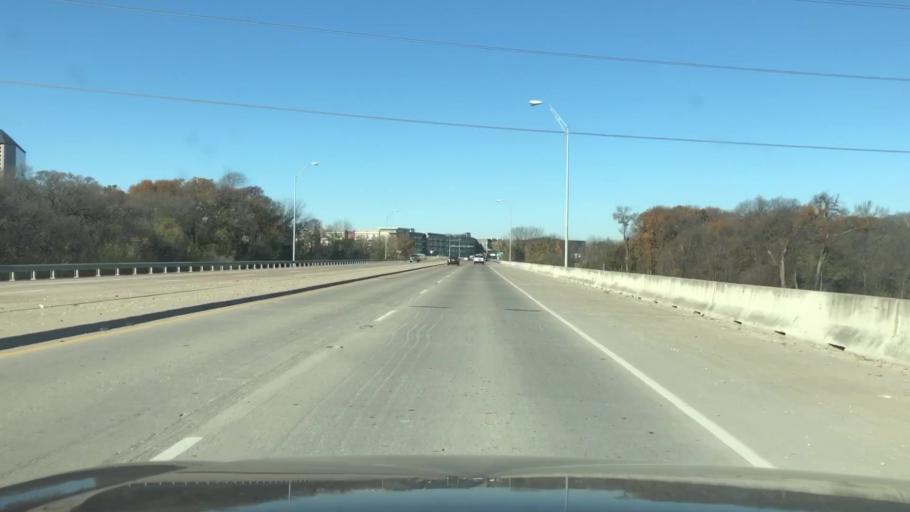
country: US
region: Texas
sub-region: Dallas County
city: Farmers Branch
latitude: 32.8732
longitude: -96.9285
